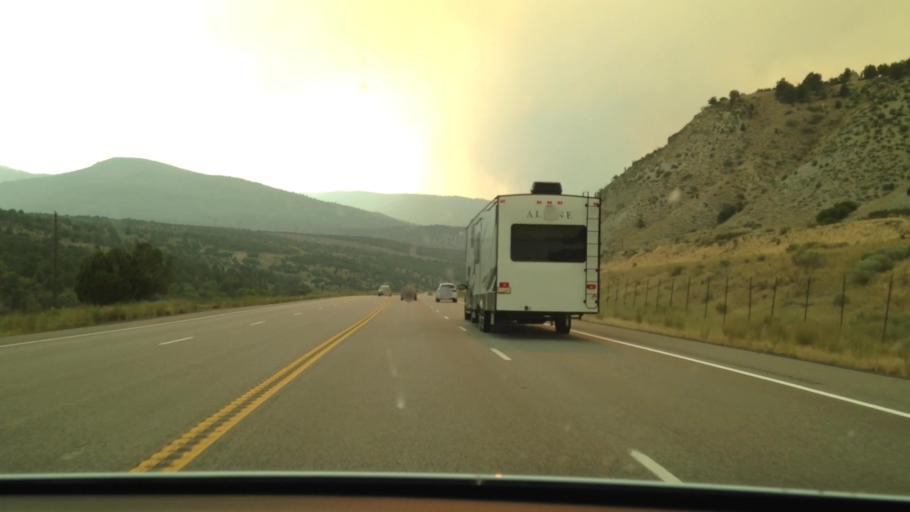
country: US
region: Utah
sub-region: Sanpete County
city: Fairview
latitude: 39.9303
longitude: -111.1752
